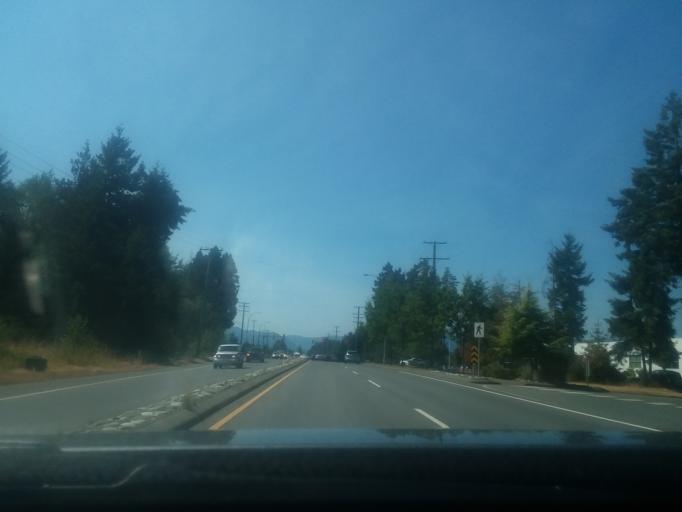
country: CA
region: British Columbia
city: Courtenay
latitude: 49.7139
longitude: -124.9592
